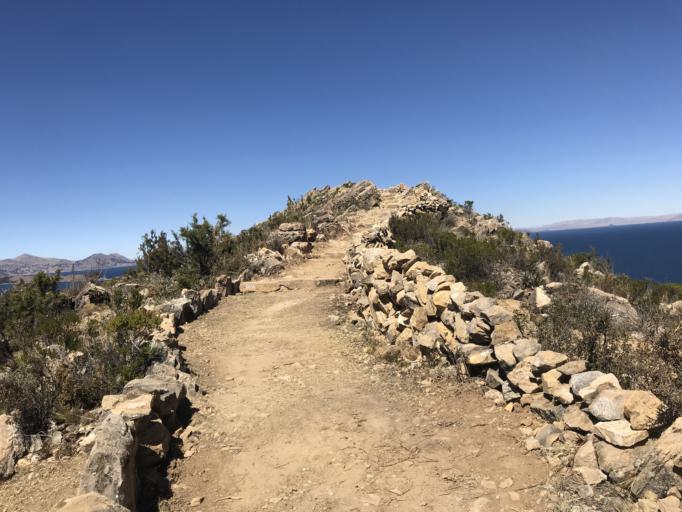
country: BO
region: La Paz
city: Yumani
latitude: -16.0473
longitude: -69.1465
